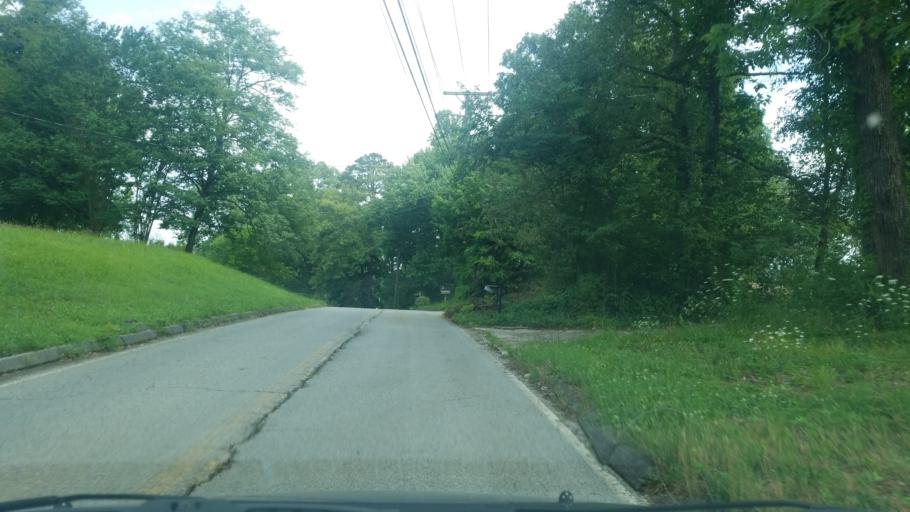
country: US
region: Tennessee
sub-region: Hamilton County
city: Apison
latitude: 35.0235
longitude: -85.0448
